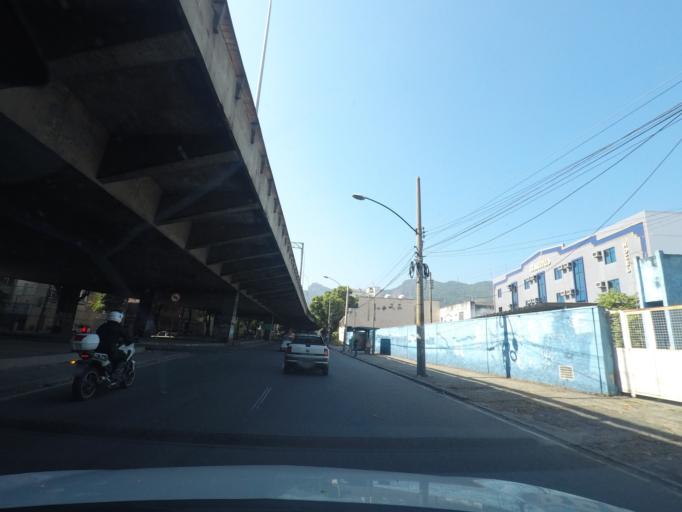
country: BR
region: Rio de Janeiro
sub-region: Rio De Janeiro
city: Rio de Janeiro
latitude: -22.9131
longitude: -43.2105
